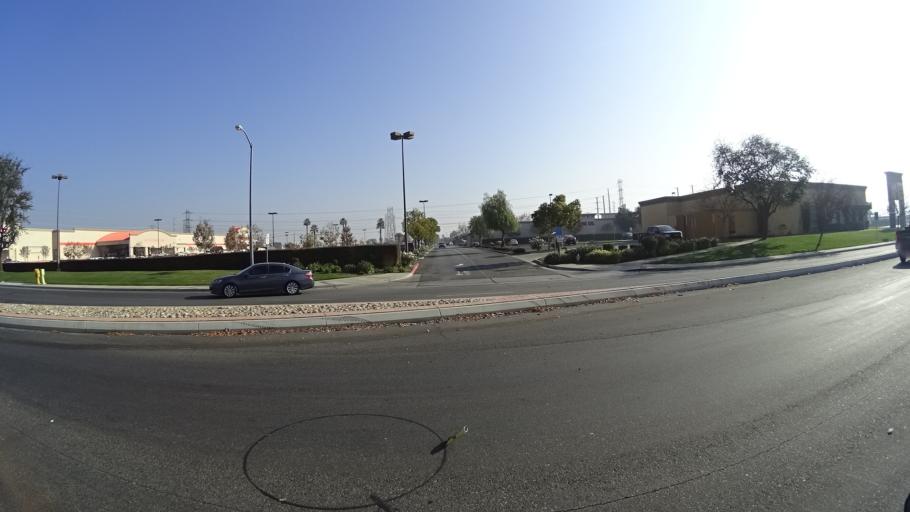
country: US
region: California
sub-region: Kern County
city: Greenacres
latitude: 35.3844
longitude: -119.1011
